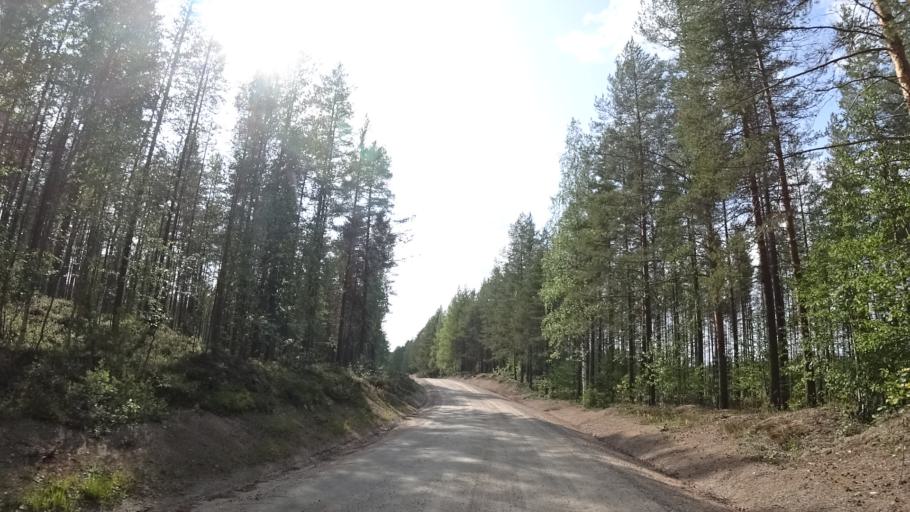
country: FI
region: North Karelia
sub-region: Pielisen Karjala
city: Lieksa
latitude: 63.5701
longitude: 30.1049
